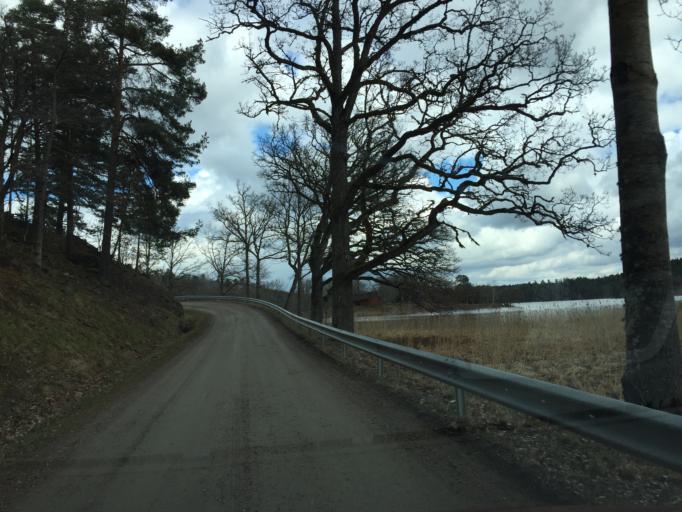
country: SE
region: Soedermanland
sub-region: Nykopings Kommun
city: Nykoping
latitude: 58.9803
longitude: 17.0052
